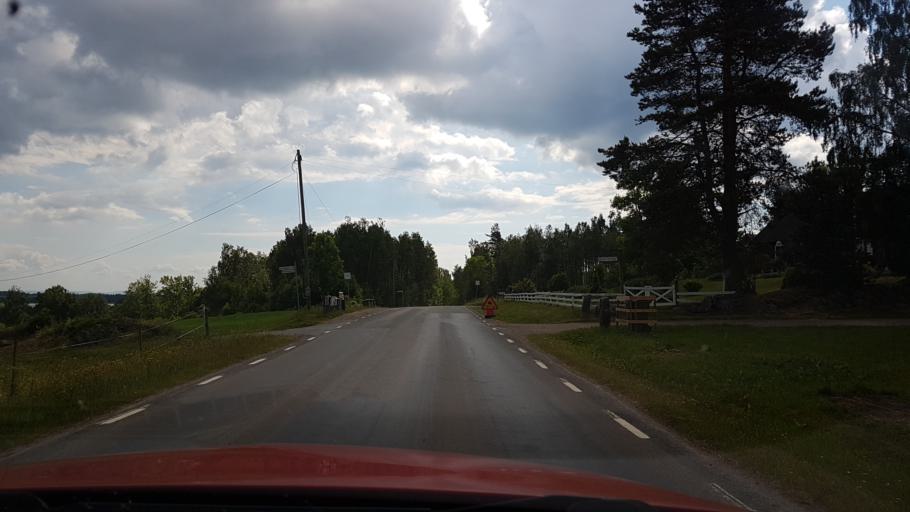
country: SE
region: Vaestra Goetaland
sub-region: Hjo Kommun
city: Hjo
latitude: 58.3111
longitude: 14.1848
